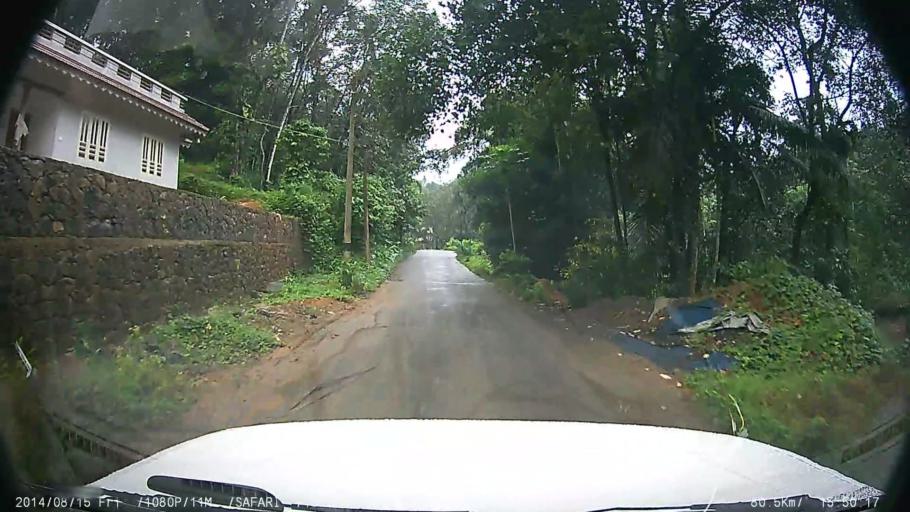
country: IN
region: Kerala
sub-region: Kottayam
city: Lalam
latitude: 9.8074
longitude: 76.7298
